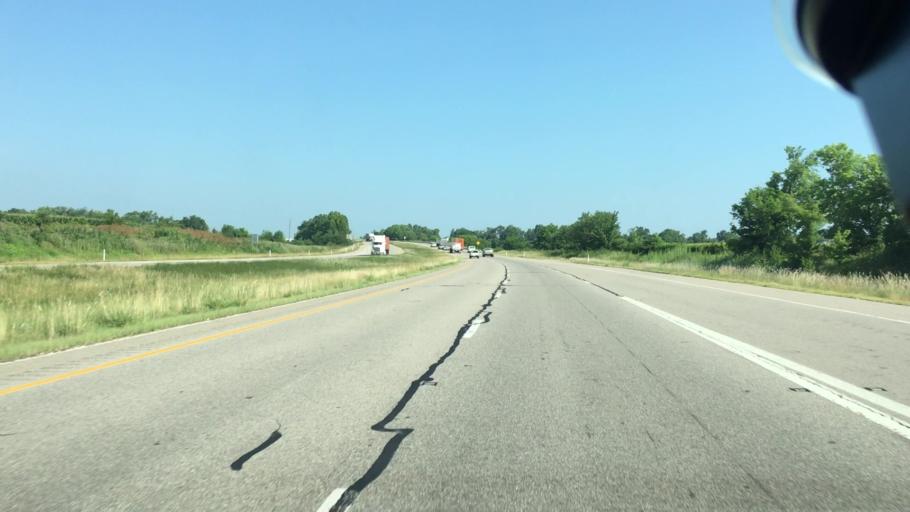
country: US
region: Indiana
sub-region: Gibson County
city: Princeton
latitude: 38.3153
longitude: -87.5701
